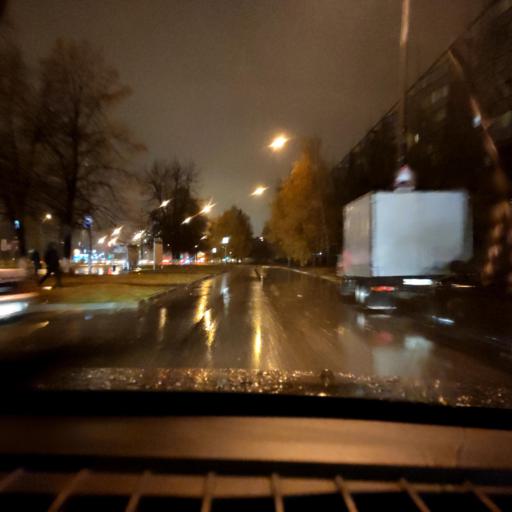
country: RU
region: Samara
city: Tol'yatti
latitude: 53.5275
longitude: 49.3017
